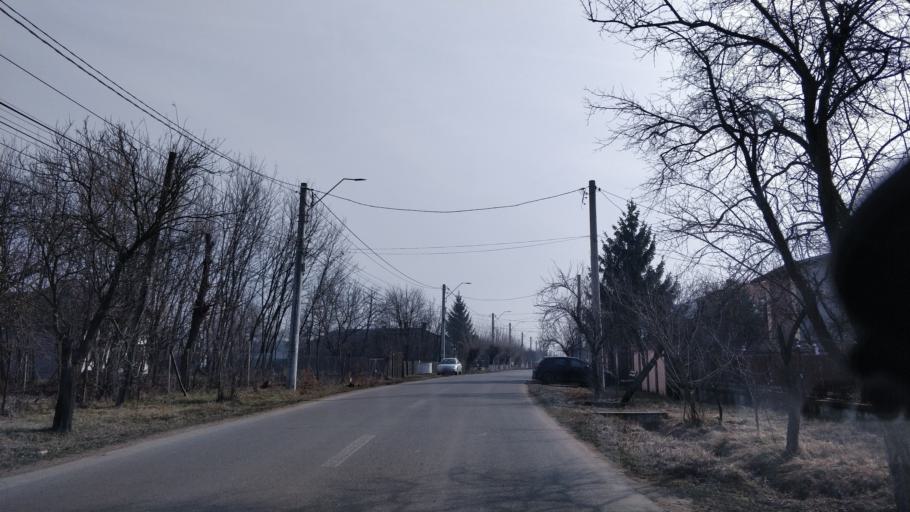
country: RO
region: Giurgiu
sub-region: Comuna Ulmi
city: Ulmi
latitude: 44.4639
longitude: 25.7762
